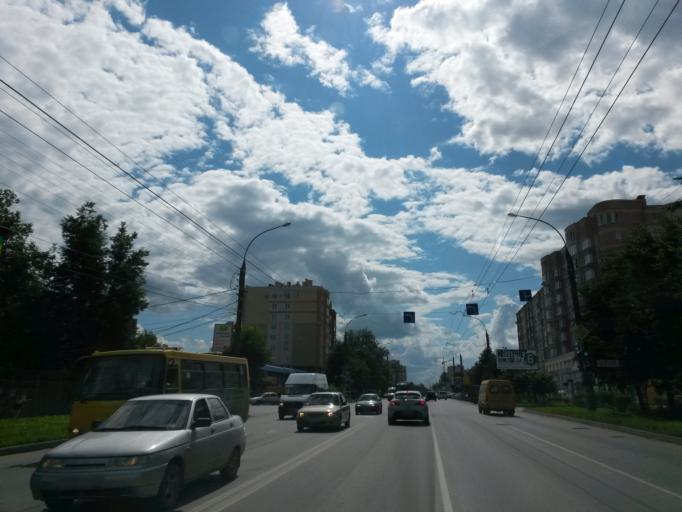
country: RU
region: Ivanovo
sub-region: Gorod Ivanovo
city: Ivanovo
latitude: 56.9910
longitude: 40.9723
